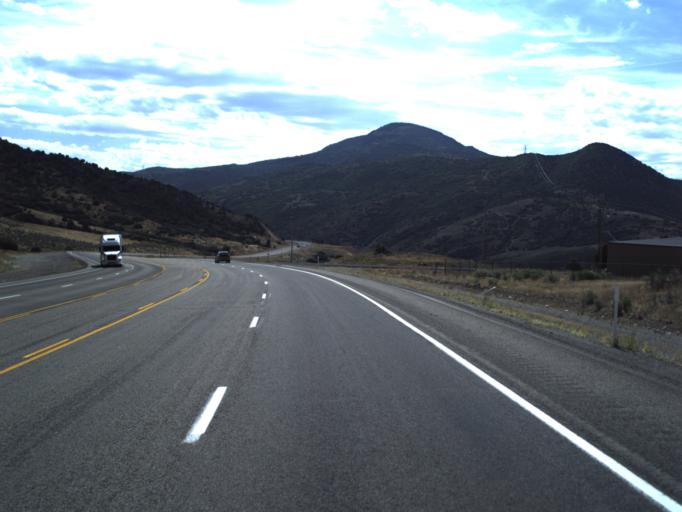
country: US
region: Utah
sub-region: Utah County
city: Mapleton
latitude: 40.0014
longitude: -111.4884
